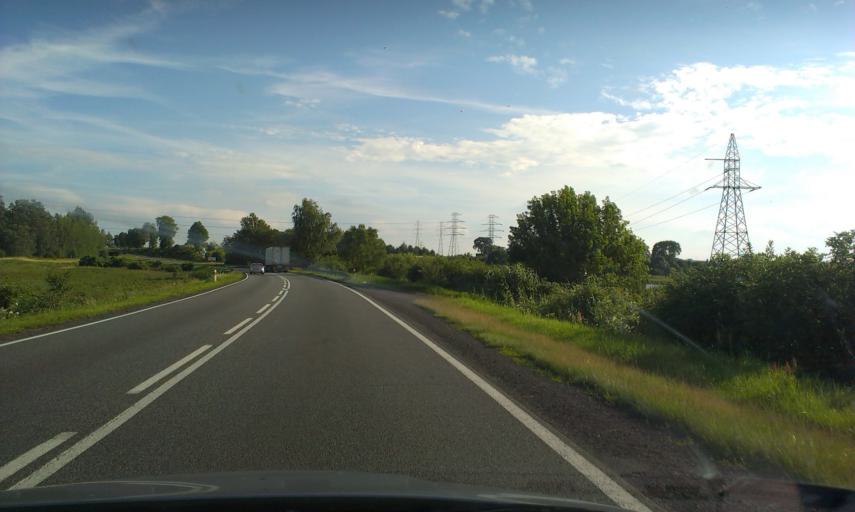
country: PL
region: Kujawsko-Pomorskie
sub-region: Powiat bydgoski
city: Biale Blota
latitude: 53.1405
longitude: 17.8792
